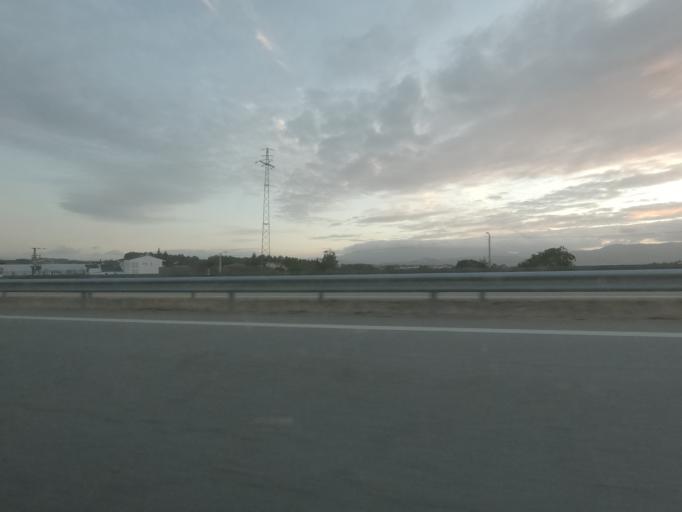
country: PT
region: Vila Real
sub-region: Vila Real
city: Vila Real
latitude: 41.2802
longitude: -7.6908
